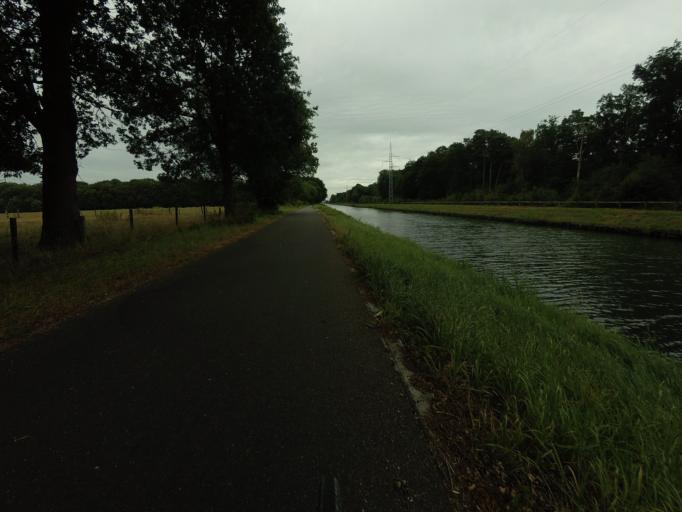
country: BE
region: Flanders
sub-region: Provincie Antwerpen
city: Brecht
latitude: 51.3224
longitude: 4.6193
